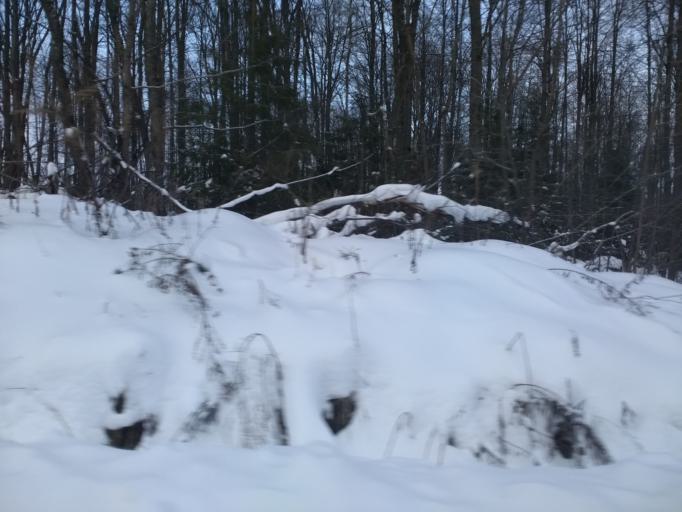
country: RU
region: Bashkortostan
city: Kudeyevskiy
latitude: 54.7126
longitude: 56.6404
